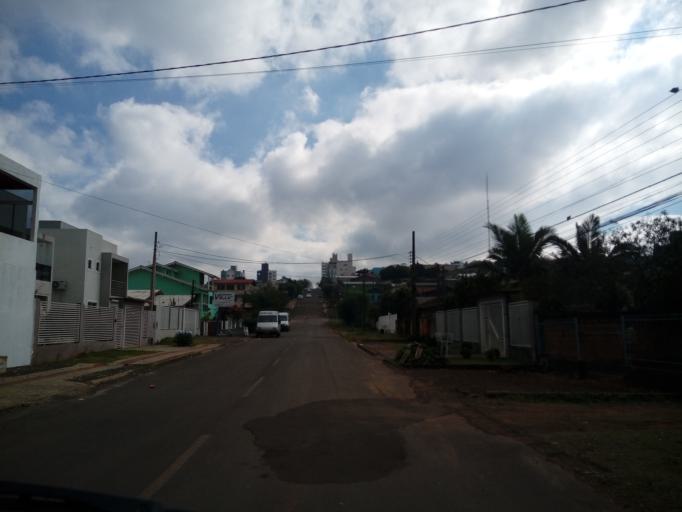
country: BR
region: Santa Catarina
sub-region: Chapeco
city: Chapeco
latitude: -27.0963
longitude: -52.5986
